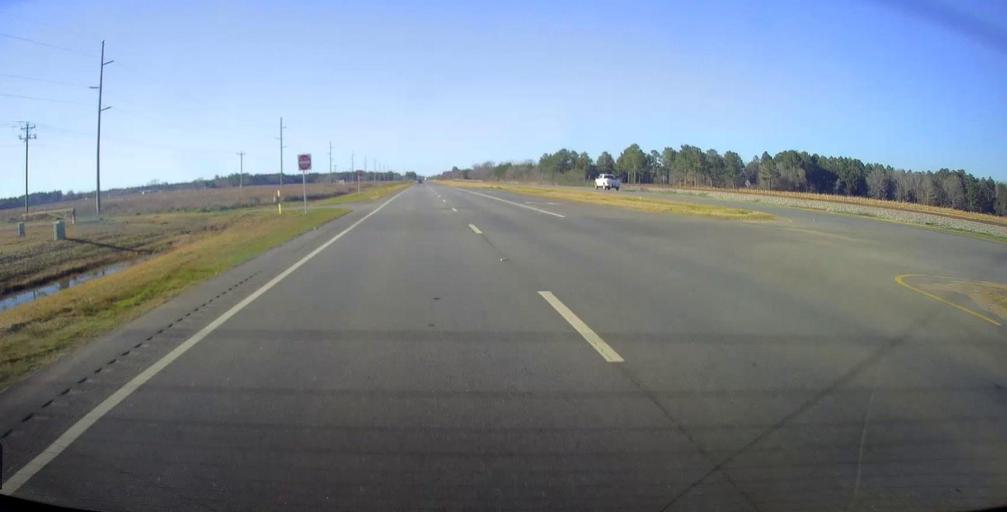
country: US
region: Georgia
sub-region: Lee County
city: Leesburg
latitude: 31.7901
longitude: -84.1997
